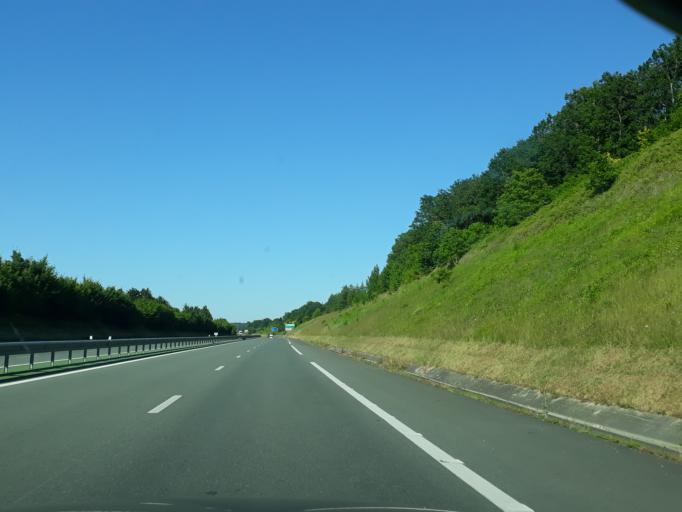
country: FR
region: Aquitaine
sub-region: Departement de la Dordogne
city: Neuvic
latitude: 45.0718
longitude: 0.4414
